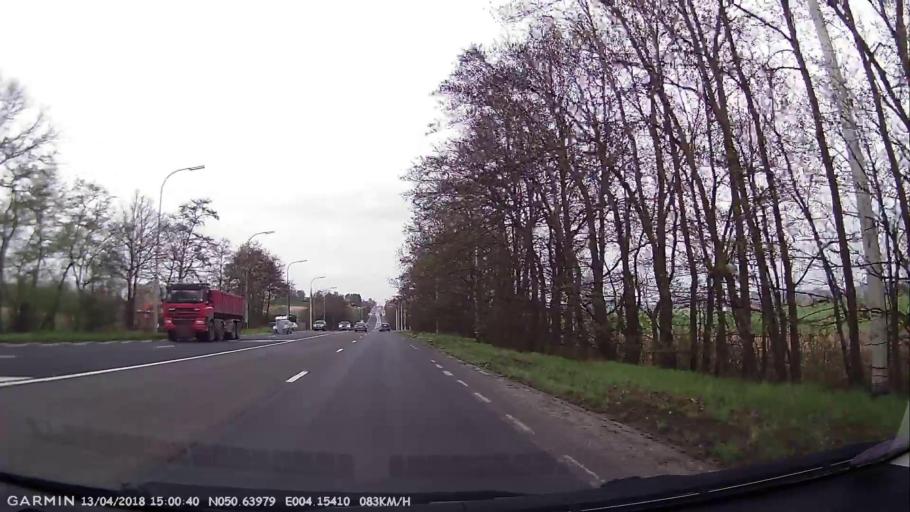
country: BE
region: Wallonia
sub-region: Province du Hainaut
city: Braine-le-Comte
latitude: 50.6400
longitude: 4.1542
